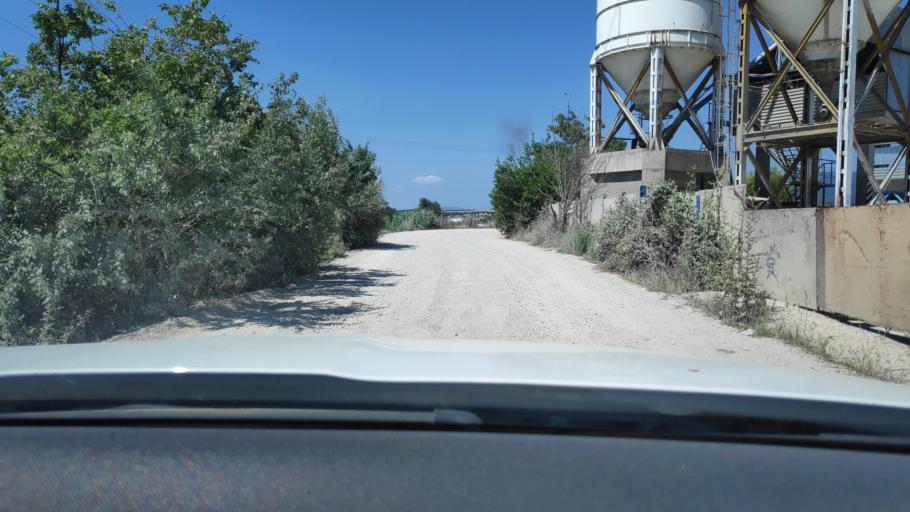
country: MK
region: Kumanovo
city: Romanovce
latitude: 42.0762
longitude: 21.7024
